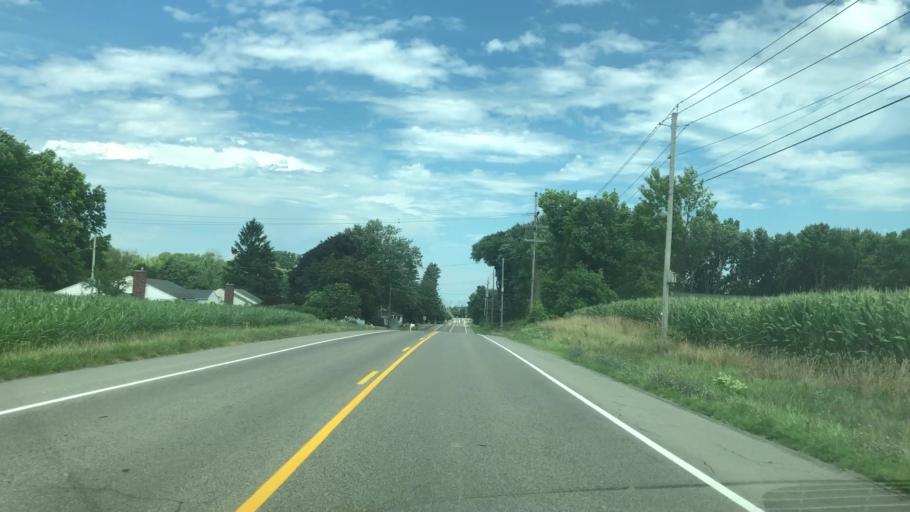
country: US
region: New York
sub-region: Monroe County
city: Webster
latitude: 43.2107
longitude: -77.4004
